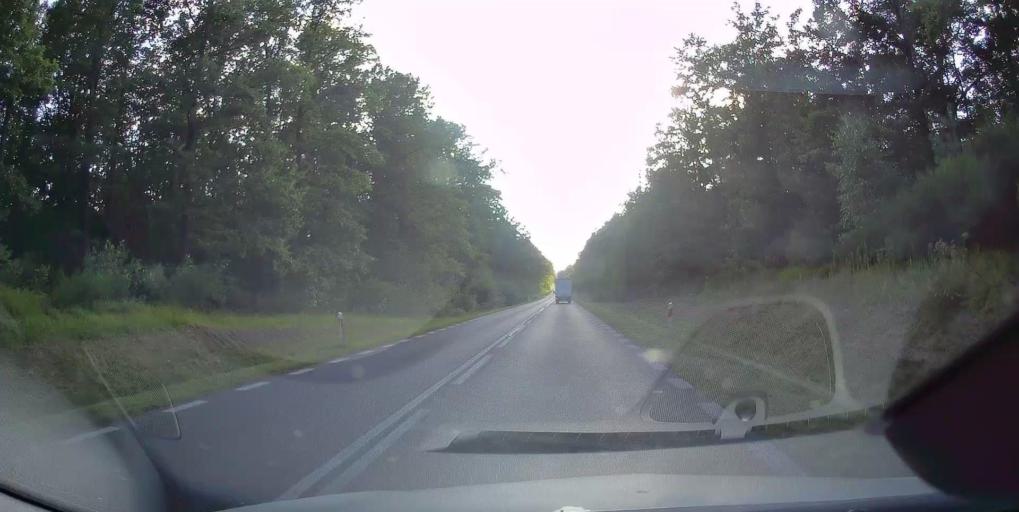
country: PL
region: Lodz Voivodeship
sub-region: Powiat rawski
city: Regnow
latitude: 51.7998
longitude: 20.4147
